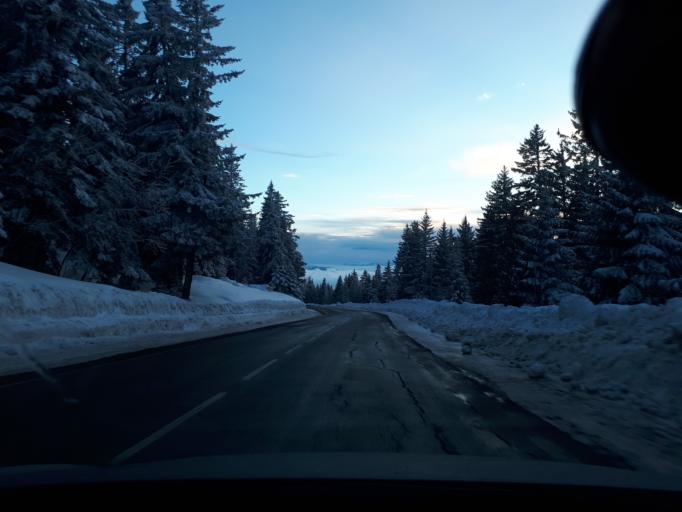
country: FR
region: Rhone-Alpes
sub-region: Departement de l'Isere
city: Vaulnaveys-le-Bas
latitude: 45.1088
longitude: 5.8729
